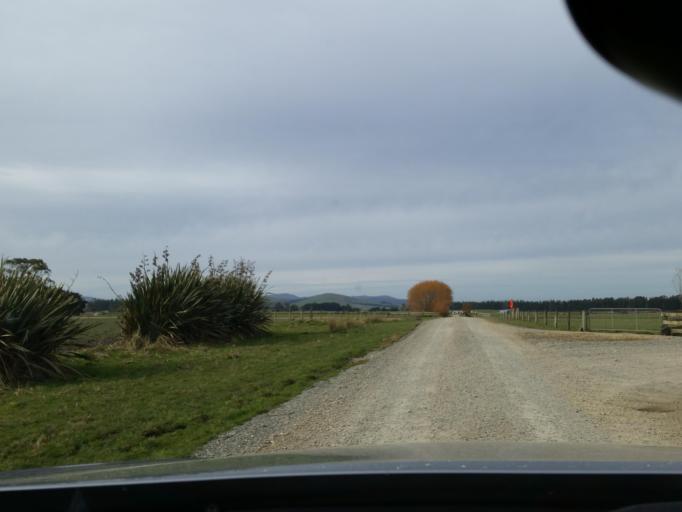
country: NZ
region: Southland
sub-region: Southland District
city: Winton
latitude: -46.2227
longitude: 168.4734
